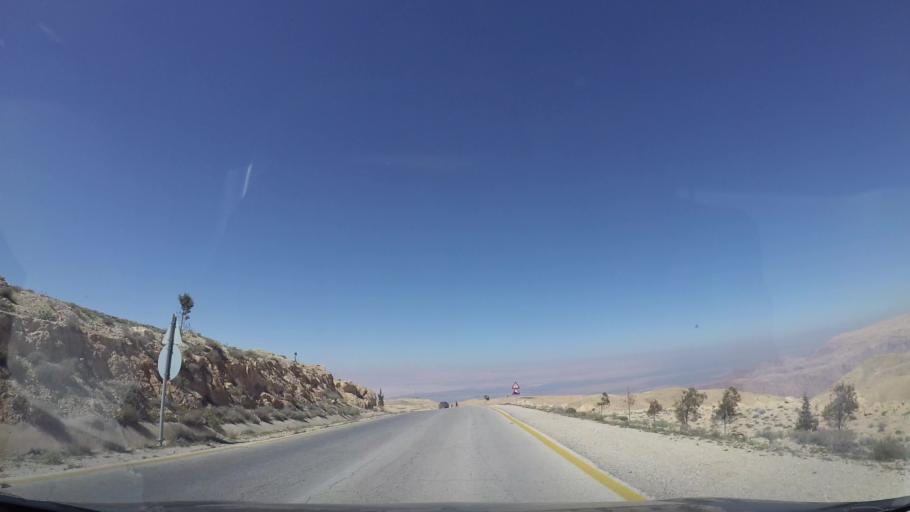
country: JO
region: Tafielah
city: At Tafilah
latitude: 30.8597
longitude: 35.5397
